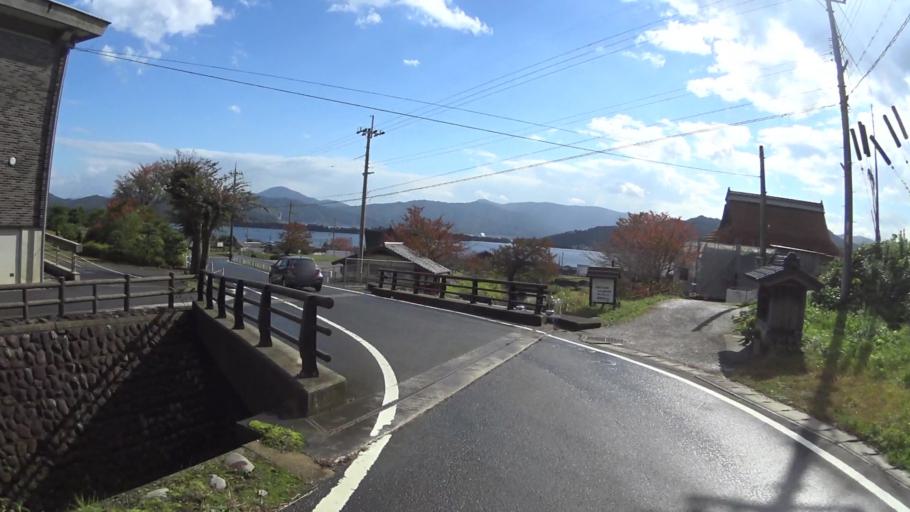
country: JP
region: Kyoto
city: Miyazu
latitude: 35.5799
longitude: 135.1780
